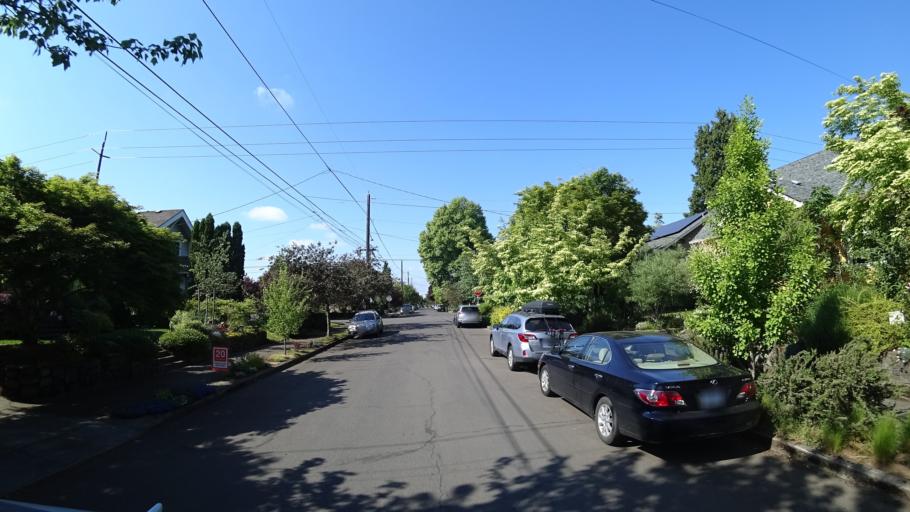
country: US
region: Oregon
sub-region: Multnomah County
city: Portland
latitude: 45.5540
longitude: -122.6439
